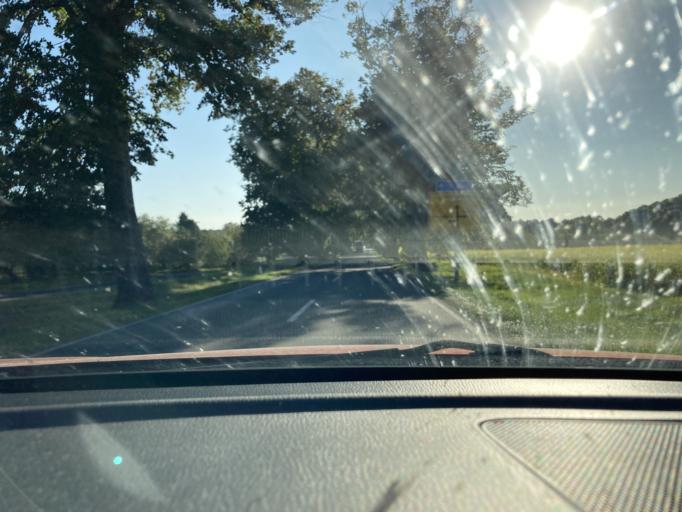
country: DE
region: Mecklenburg-Vorpommern
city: Alt-Sanitz
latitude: 53.7542
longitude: 13.6270
